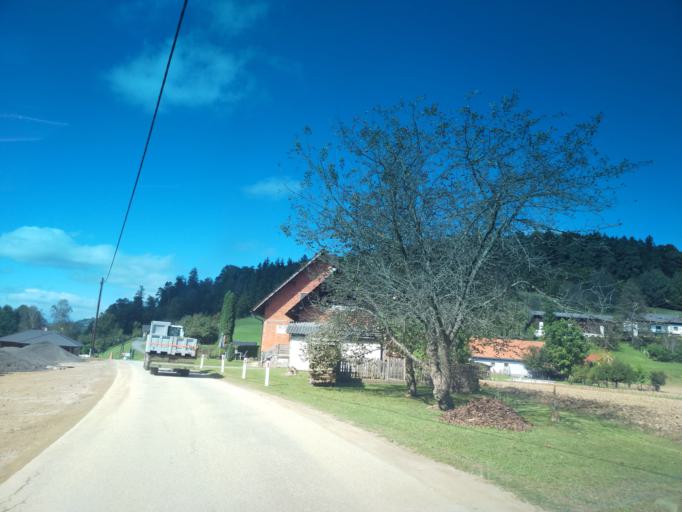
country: AT
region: Styria
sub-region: Politischer Bezirk Leibnitz
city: Grossklein
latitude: 46.7335
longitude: 15.4540
